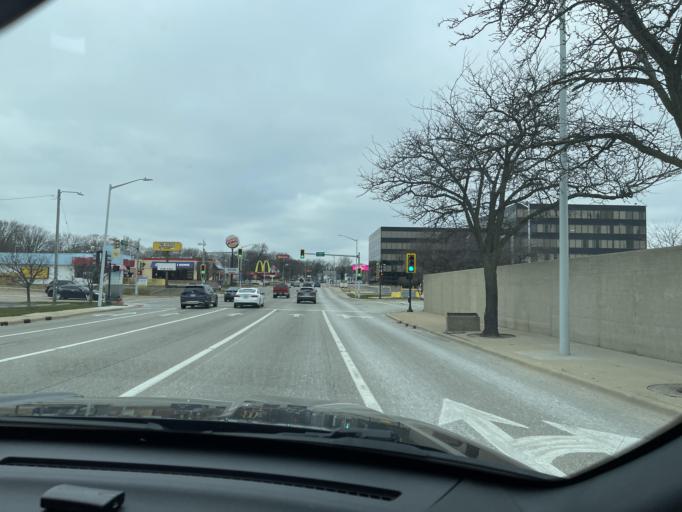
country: US
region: Illinois
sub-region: Sangamon County
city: Springfield
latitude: 39.8030
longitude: -89.6591
